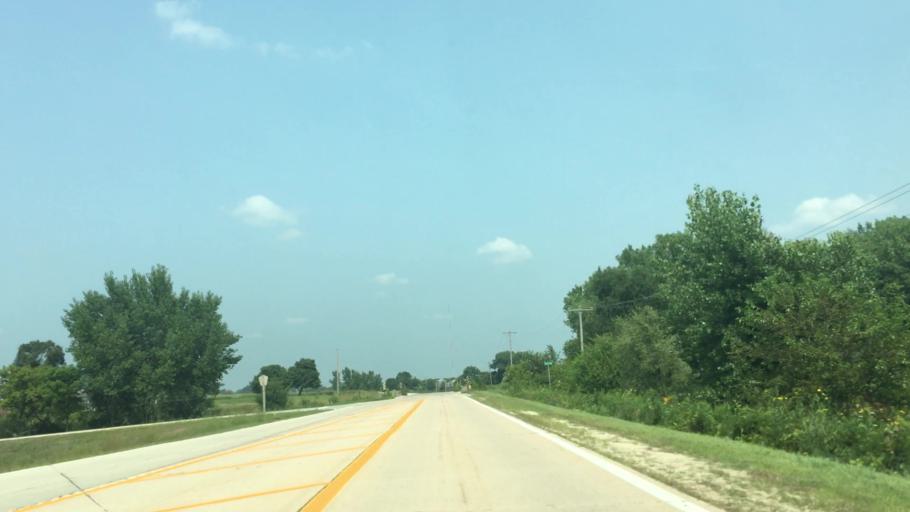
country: US
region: Iowa
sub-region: Fayette County
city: Oelwein
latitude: 42.6608
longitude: -91.8976
